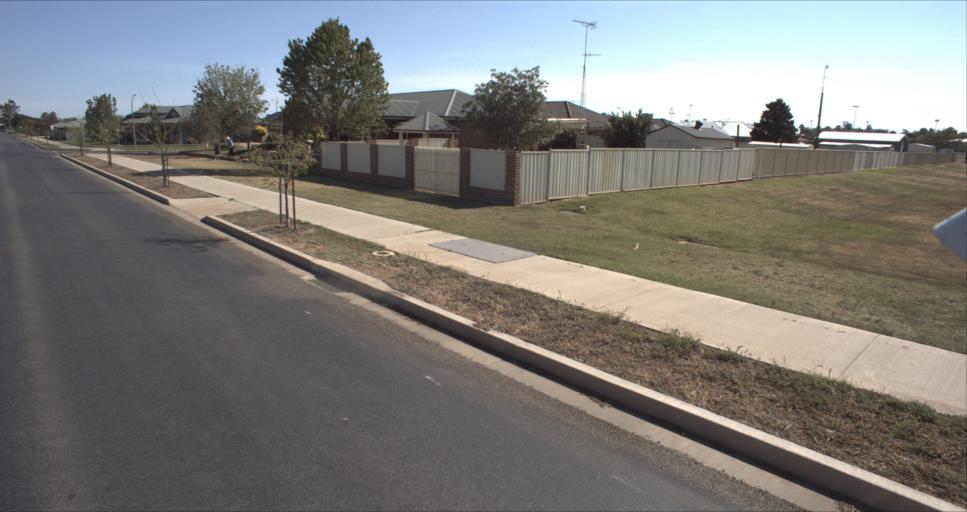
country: AU
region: New South Wales
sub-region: Leeton
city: Leeton
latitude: -34.5520
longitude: 146.4170
